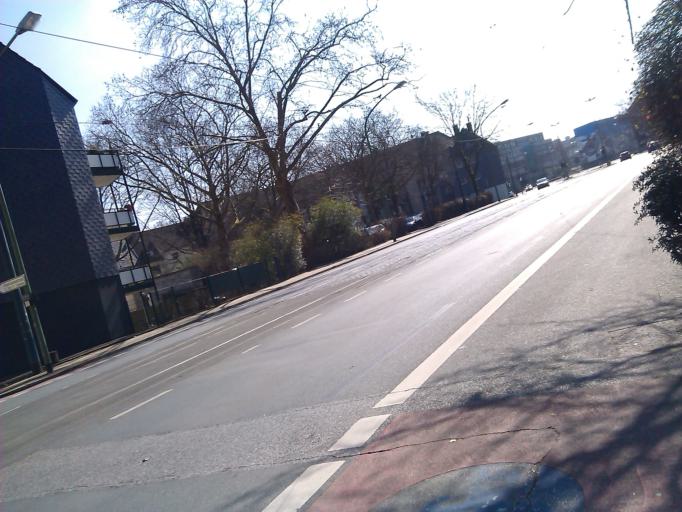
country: DE
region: North Rhine-Westphalia
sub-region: Regierungsbezirk Dusseldorf
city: Essen
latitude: 51.4587
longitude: 7.0216
